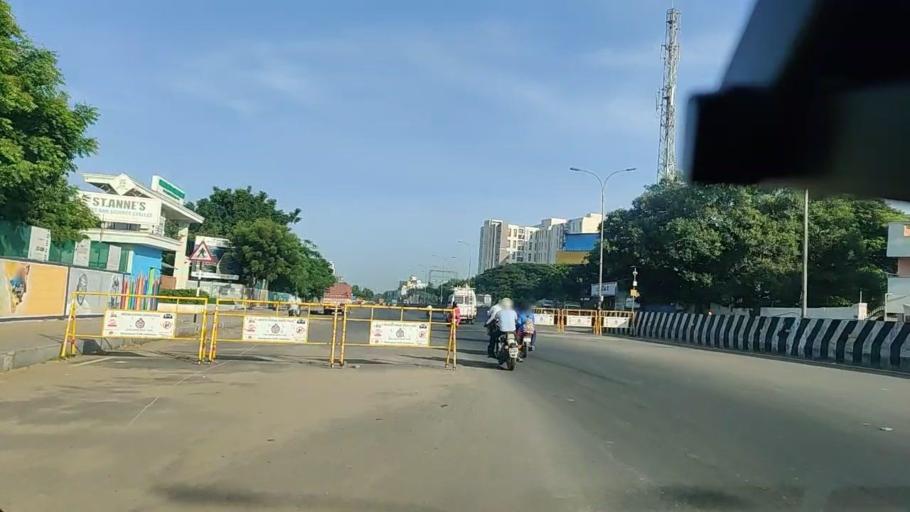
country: IN
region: Tamil Nadu
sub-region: Thiruvallur
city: Chinnasekkadu
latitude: 13.1338
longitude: 80.2345
